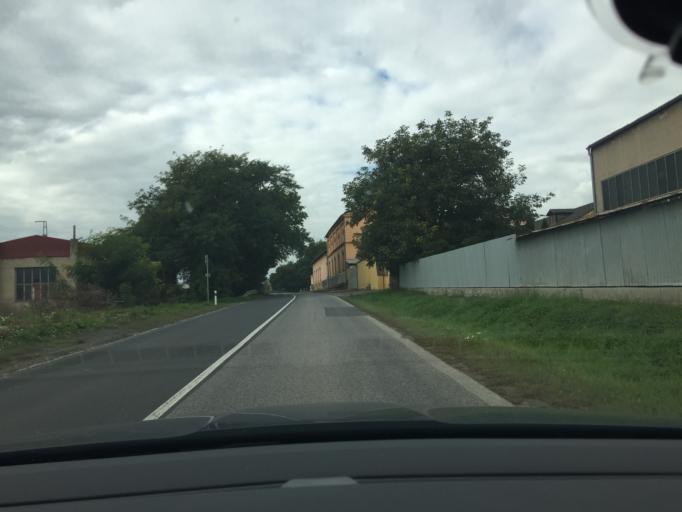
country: CZ
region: Ustecky
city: Terezin
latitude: 50.5318
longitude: 14.1612
